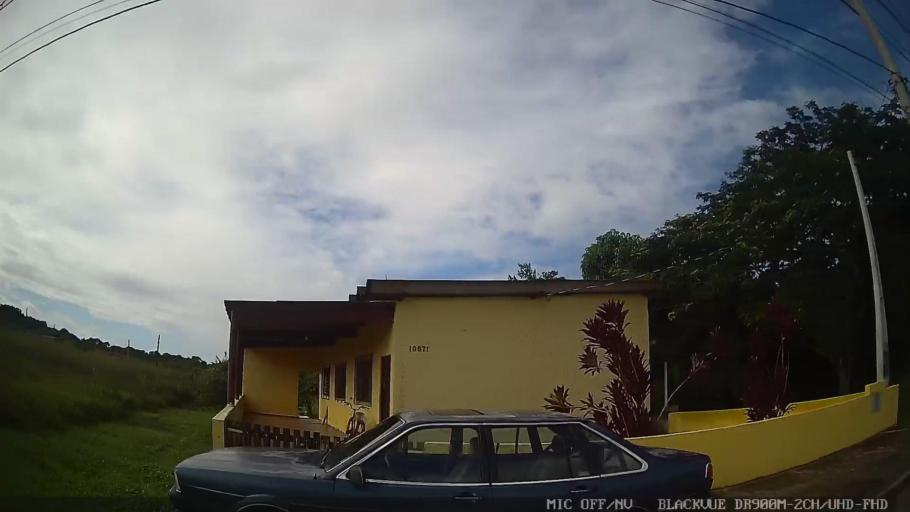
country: BR
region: Sao Paulo
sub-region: Itanhaem
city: Itanhaem
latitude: -24.2282
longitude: -46.8912
